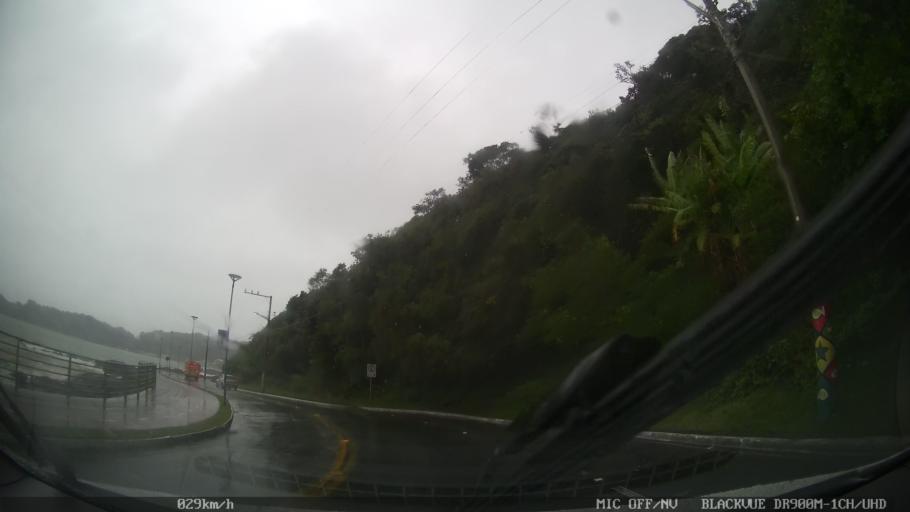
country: BR
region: Santa Catarina
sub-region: Itajai
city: Itajai
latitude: -26.9239
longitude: -48.6351
